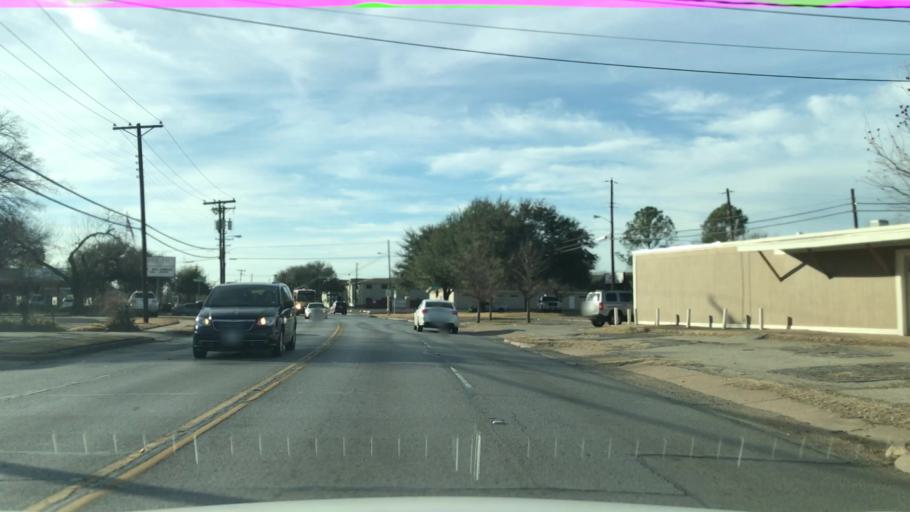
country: US
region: Texas
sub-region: Dallas County
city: Irving
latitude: 32.8221
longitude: -96.9612
